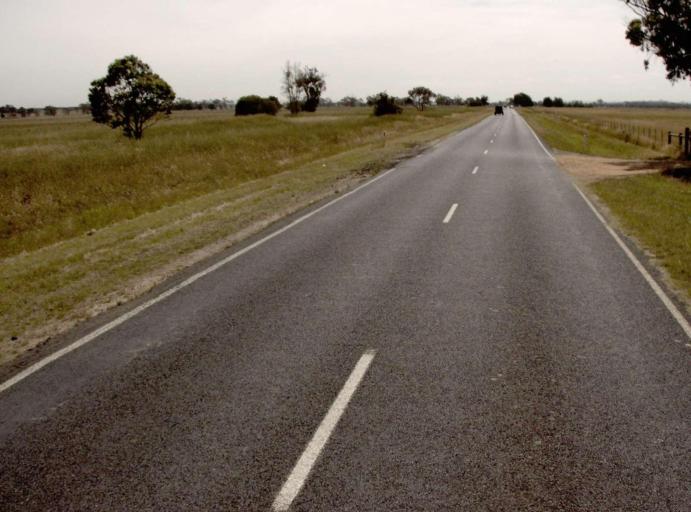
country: AU
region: Victoria
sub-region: Wellington
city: Heyfield
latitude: -38.1552
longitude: 146.8419
